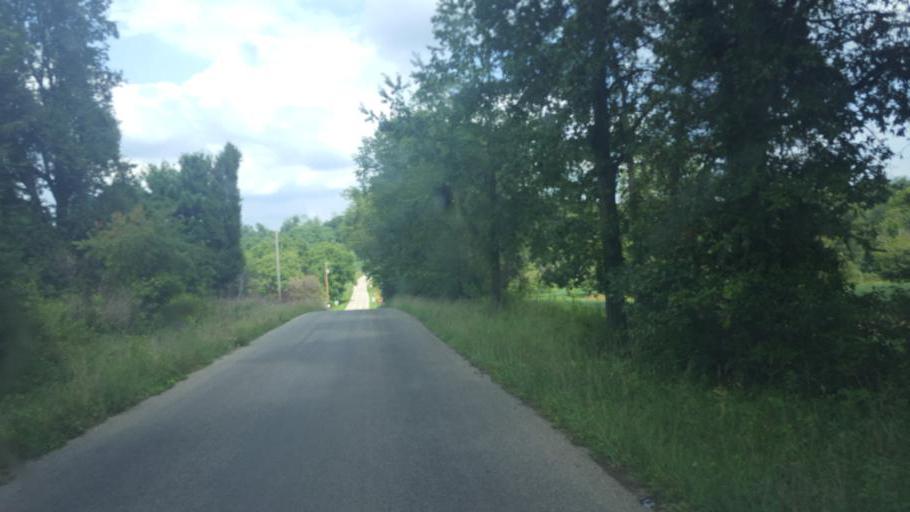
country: US
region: Ohio
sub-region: Knox County
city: Gambier
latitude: 40.3798
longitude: -82.3166
